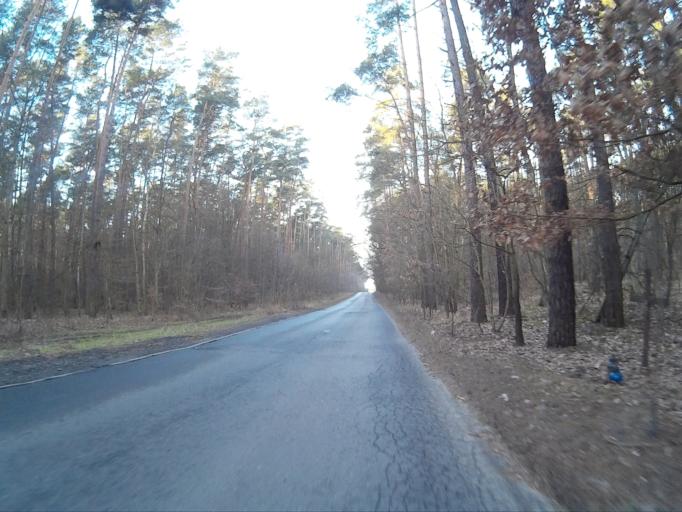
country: PL
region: Kujawsko-Pomorskie
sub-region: Powiat bydgoski
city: Osielsko
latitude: 53.1609
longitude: 18.0649
